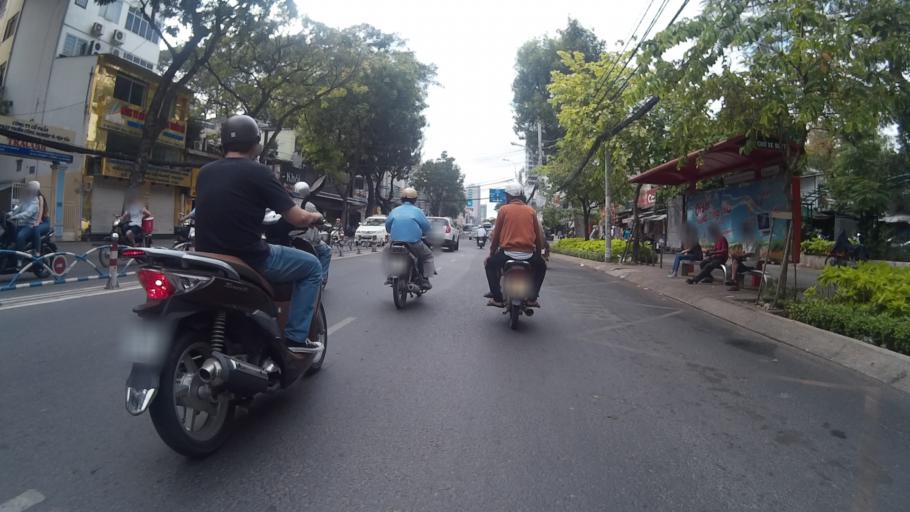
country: VN
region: Ho Chi Minh City
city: Quan Ba
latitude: 10.7729
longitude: 106.6910
